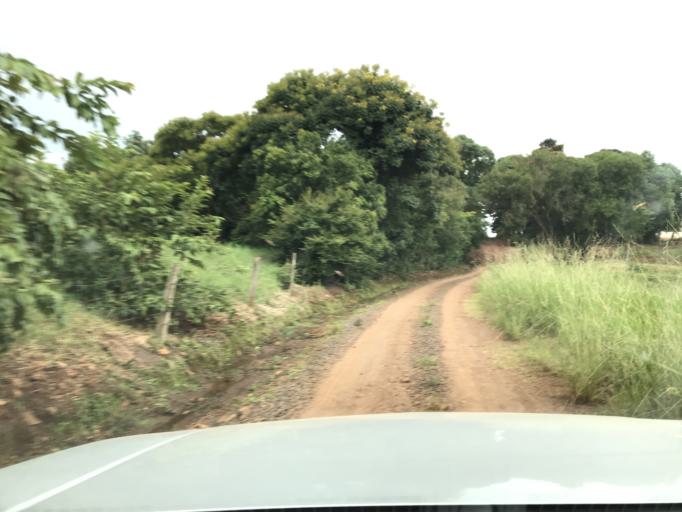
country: BR
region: Parana
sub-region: Palotina
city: Palotina
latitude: -24.2726
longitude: -53.7871
